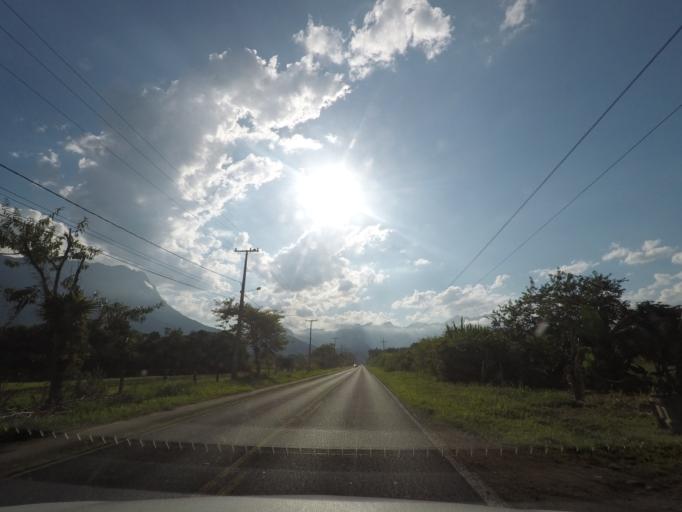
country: BR
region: Parana
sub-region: Antonina
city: Antonina
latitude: -25.4558
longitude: -48.8605
